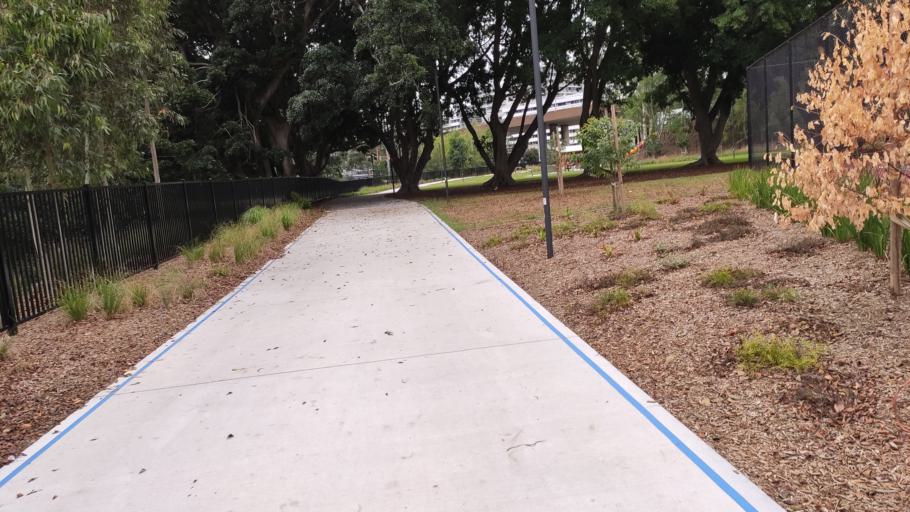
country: AU
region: New South Wales
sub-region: Strathfield
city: Homebush
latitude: -33.8628
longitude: 151.0866
